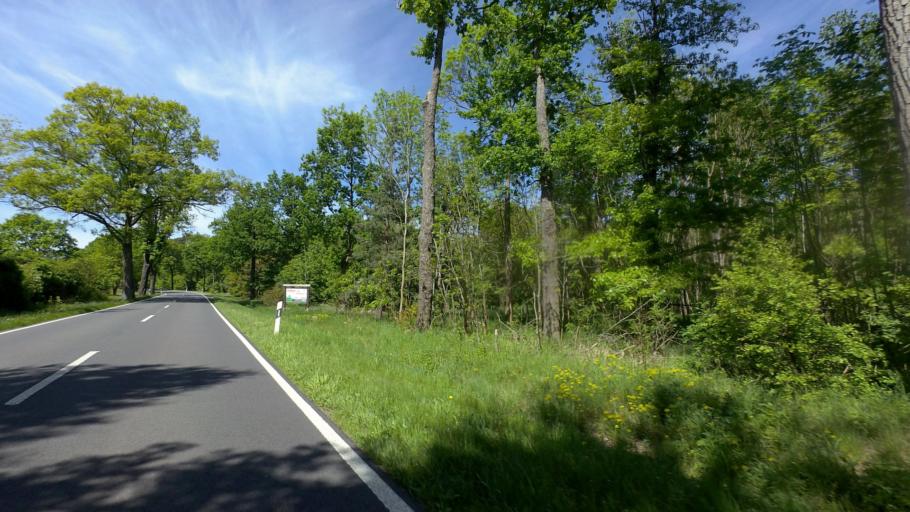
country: DE
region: Brandenburg
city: Baruth
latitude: 52.0810
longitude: 13.4506
